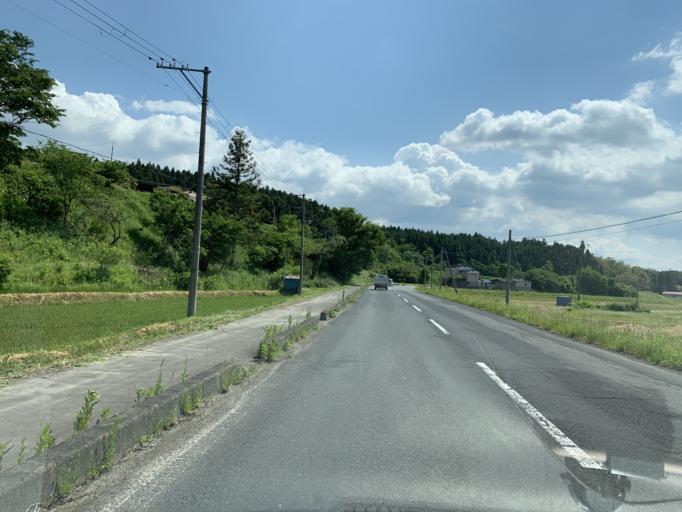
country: JP
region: Miyagi
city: Furukawa
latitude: 38.6902
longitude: 140.9448
